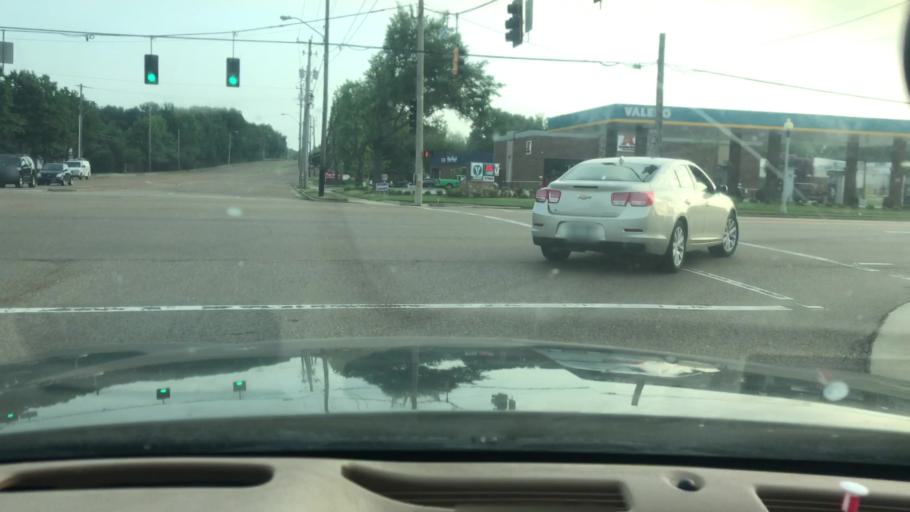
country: US
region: Tennessee
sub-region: Shelby County
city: Bartlett
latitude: 35.2046
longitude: -89.8641
